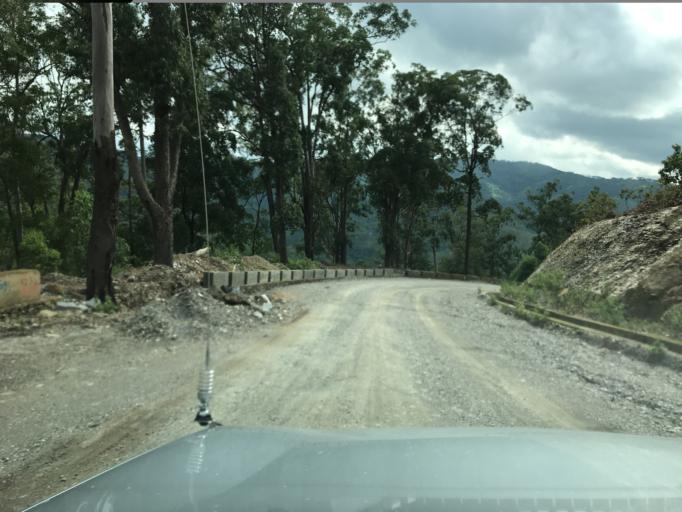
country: TL
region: Aileu
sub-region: Aileu Villa
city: Aileu
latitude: -8.6636
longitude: 125.5412
